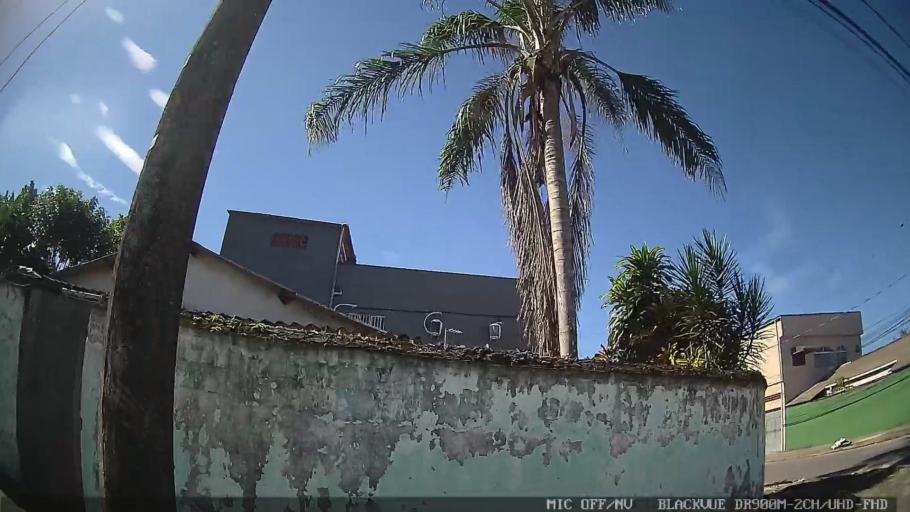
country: BR
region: Sao Paulo
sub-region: Santos
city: Santos
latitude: -23.9519
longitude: -46.2951
